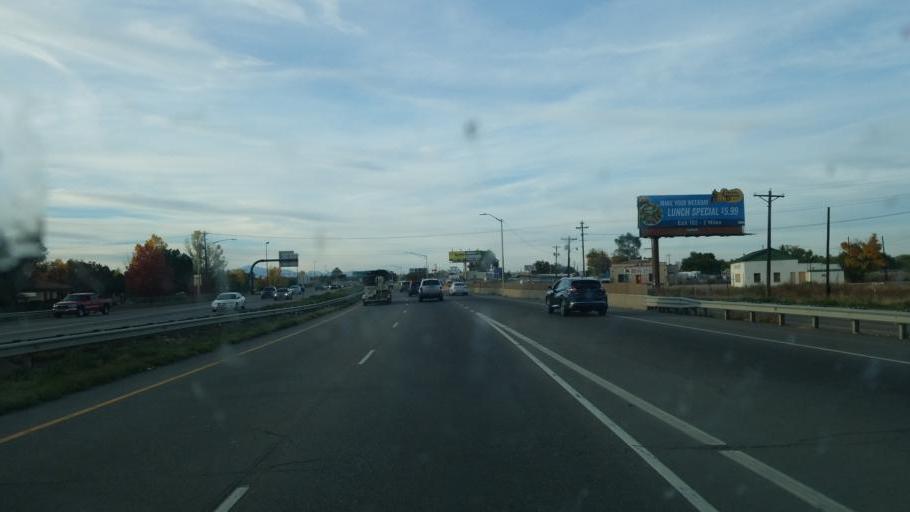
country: US
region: Colorado
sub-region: Pueblo County
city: Pueblo
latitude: 38.2899
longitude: -104.6070
